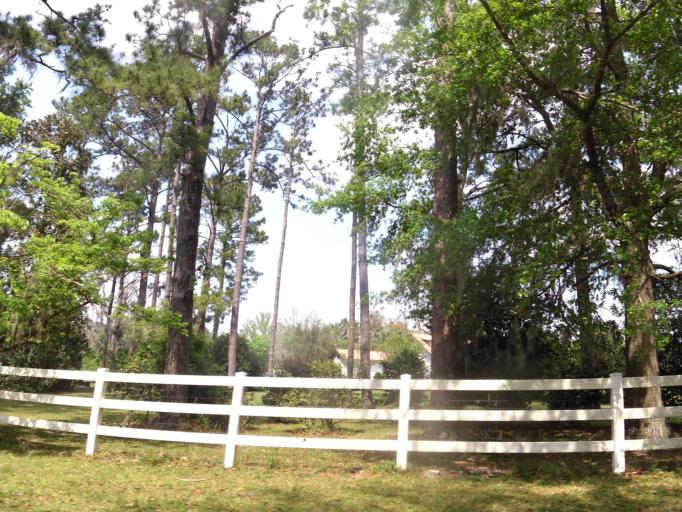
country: US
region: Georgia
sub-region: Camden County
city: Kingsland
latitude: 30.7811
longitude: -81.6893
